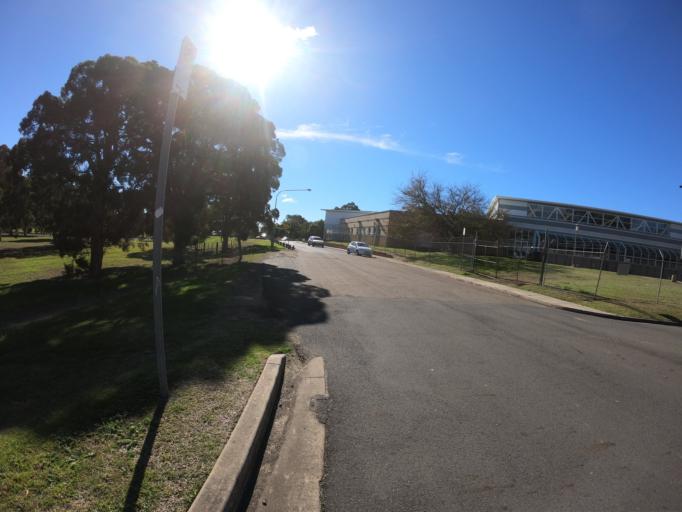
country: AU
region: New South Wales
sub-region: Hawkesbury
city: South Windsor
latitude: -33.6224
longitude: 150.7999
